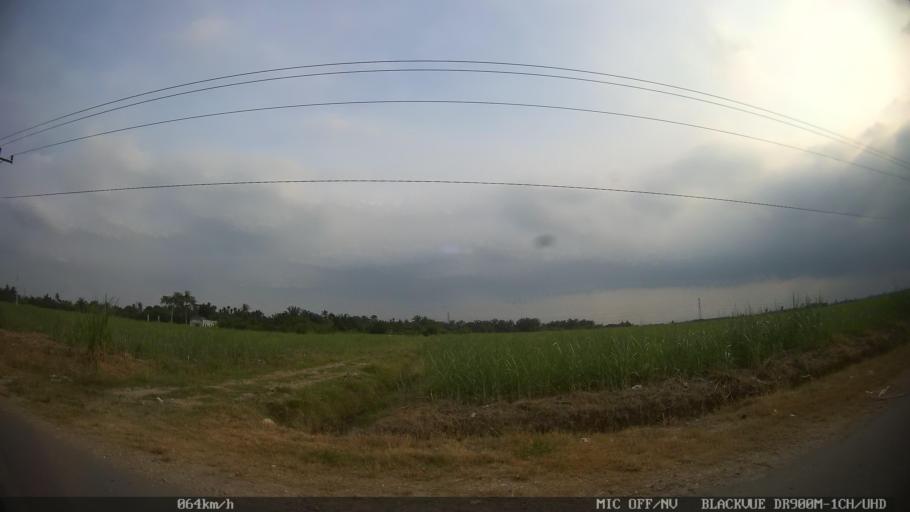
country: ID
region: North Sumatra
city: Binjai
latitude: 3.5895
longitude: 98.5452
